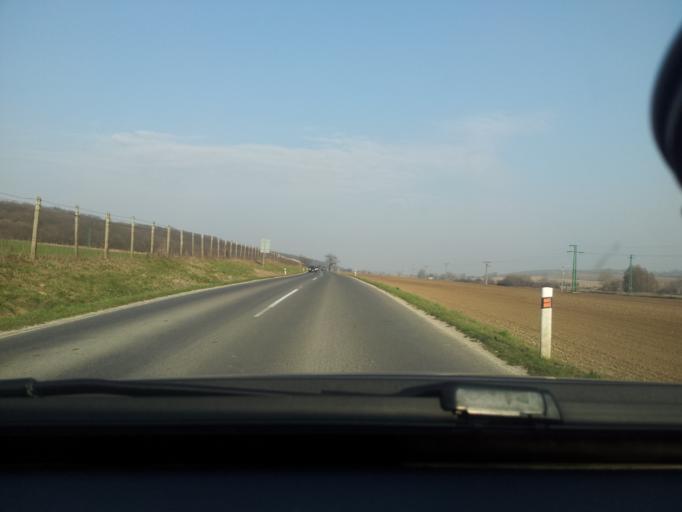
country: SK
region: Trnavsky
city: Hlohovec
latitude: 48.3879
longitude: 17.8644
